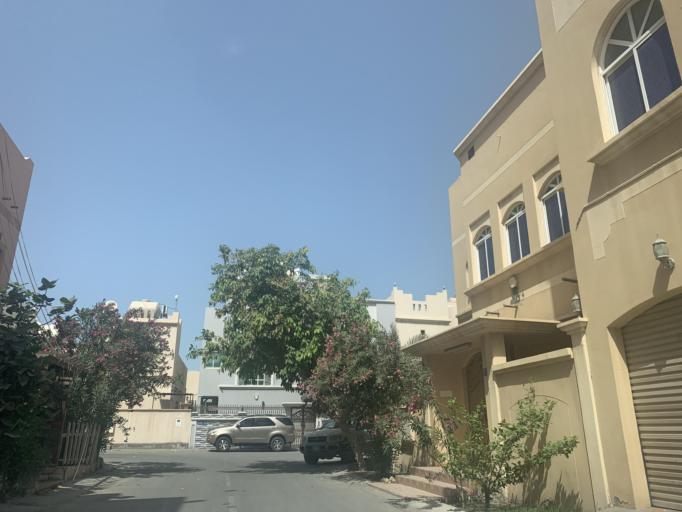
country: BH
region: Northern
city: Sitrah
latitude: 26.1698
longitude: 50.6159
